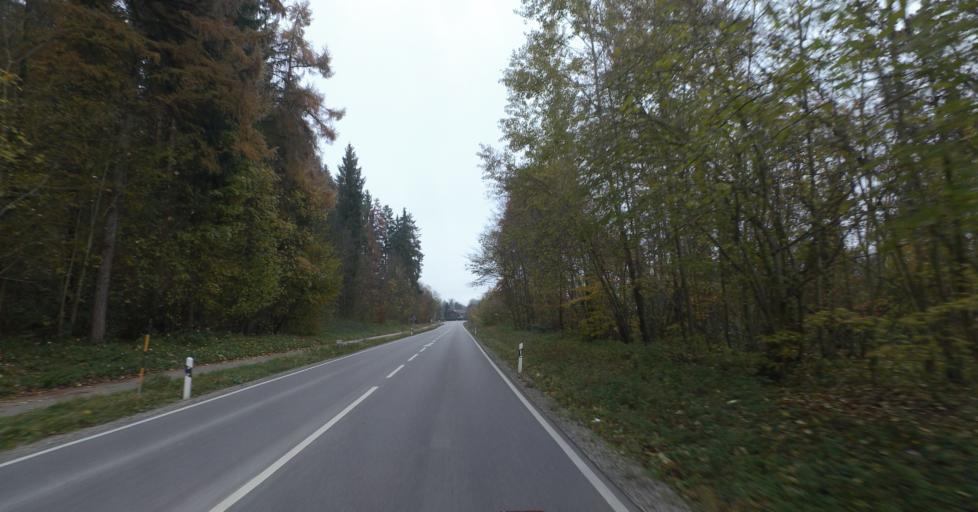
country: DE
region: Bavaria
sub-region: Upper Bavaria
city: Trostberg an der Alz
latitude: 48.0408
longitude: 12.5616
